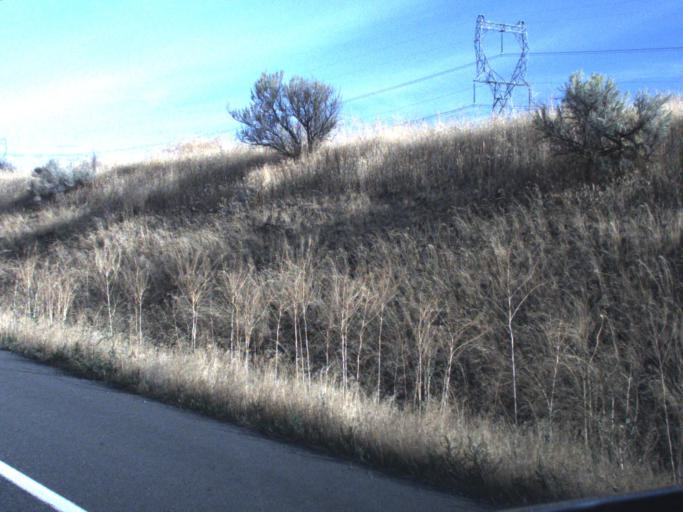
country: US
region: Oregon
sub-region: Morrow County
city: Irrigon
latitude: 45.9437
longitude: -119.5288
